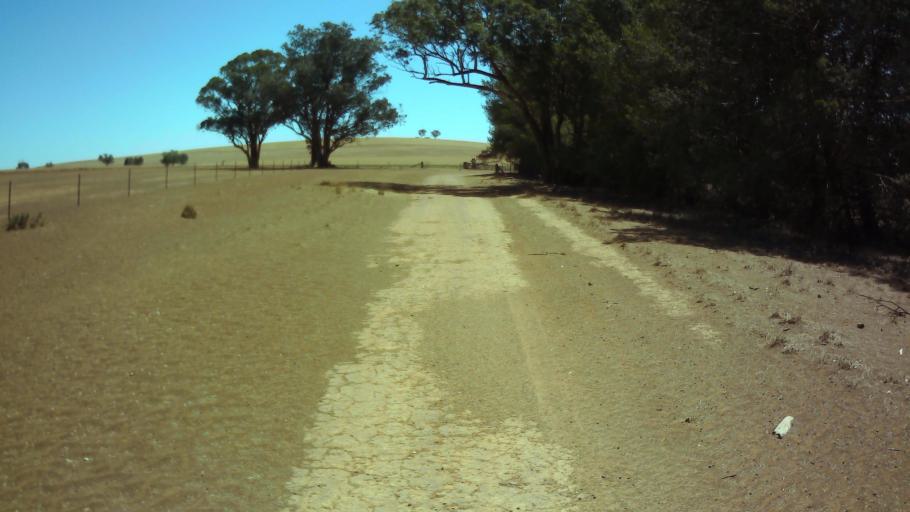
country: AU
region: New South Wales
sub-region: Weddin
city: Grenfell
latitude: -33.9831
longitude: 148.1643
